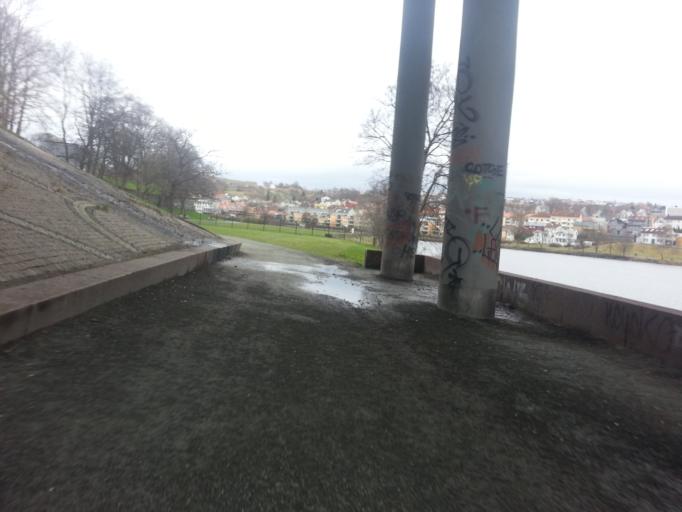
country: NO
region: Sor-Trondelag
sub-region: Trondheim
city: Trondheim
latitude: 63.4247
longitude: 10.3936
